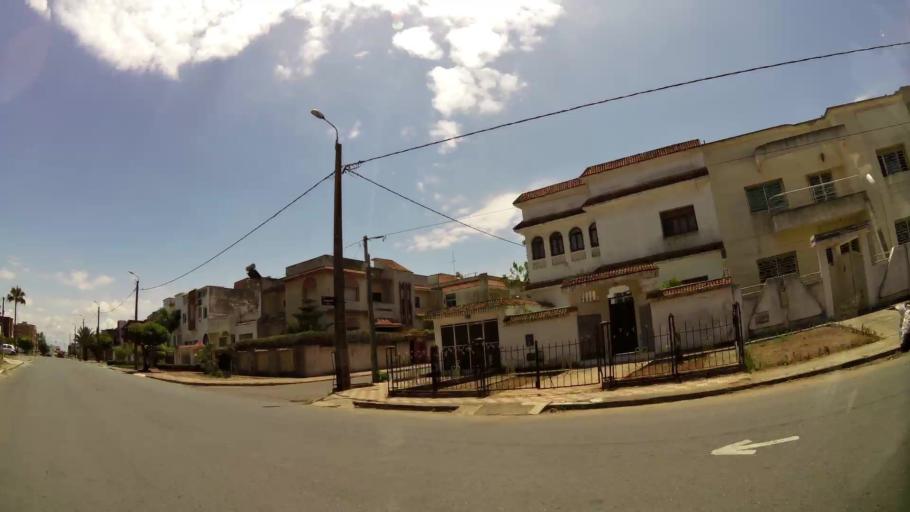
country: MA
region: Gharb-Chrarda-Beni Hssen
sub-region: Kenitra Province
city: Kenitra
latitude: 34.2657
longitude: -6.6197
